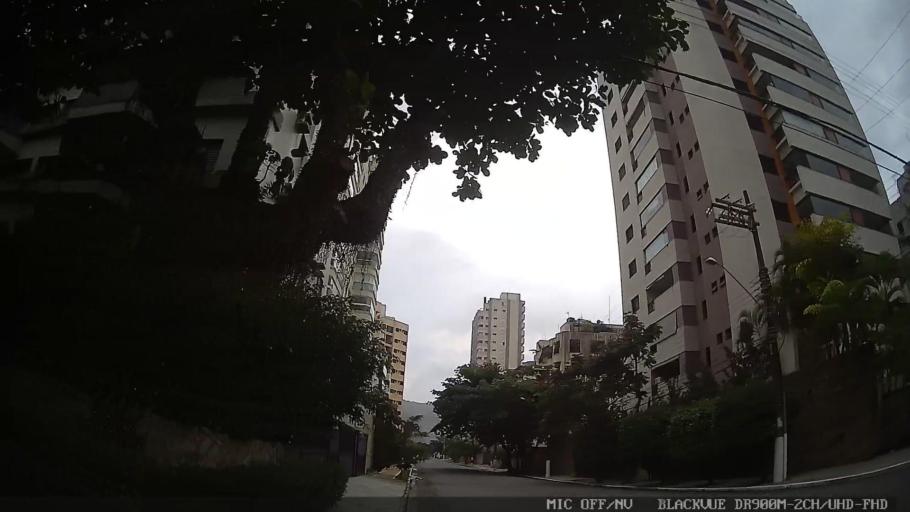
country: BR
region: Sao Paulo
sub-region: Guaruja
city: Guaruja
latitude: -23.9816
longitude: -46.2231
